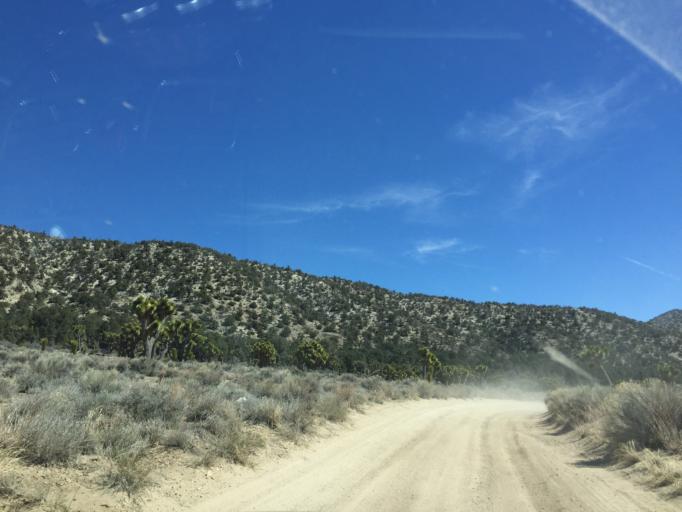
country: US
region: California
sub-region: San Bernardino County
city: Big Bear City
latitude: 34.2556
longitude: -116.7135
